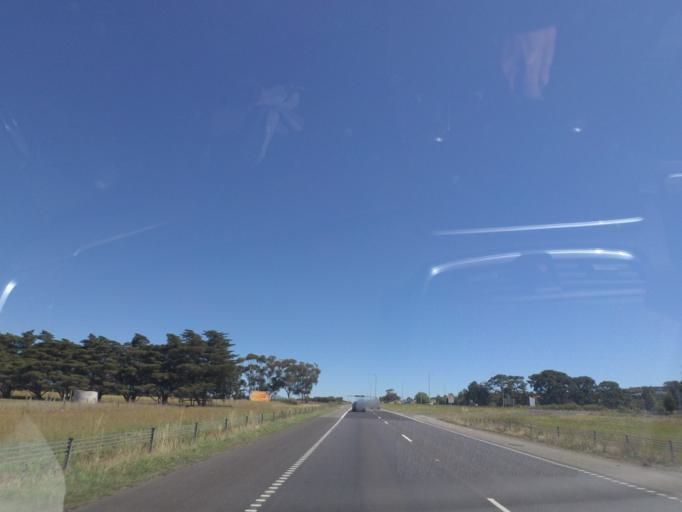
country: AU
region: Victoria
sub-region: Hume
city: Craigieburn
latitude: -37.5623
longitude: 144.9426
